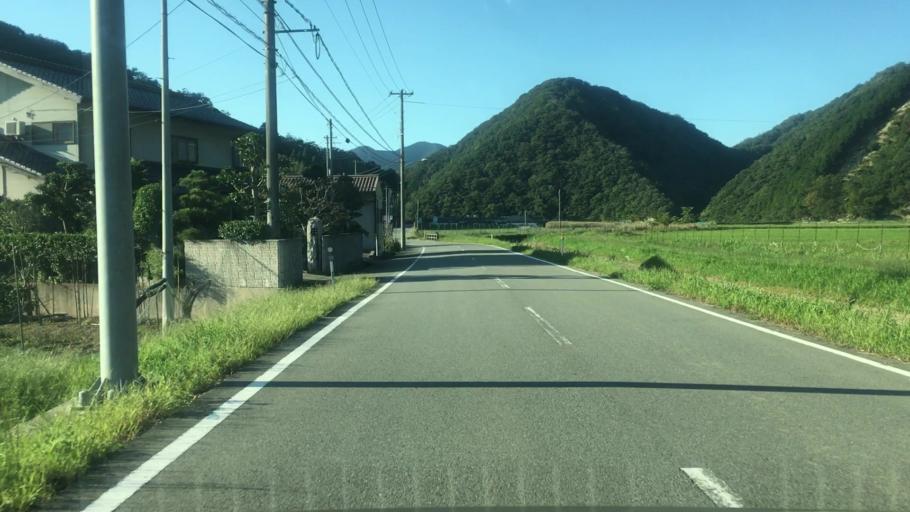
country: JP
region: Hyogo
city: Toyooka
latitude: 35.6115
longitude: 134.8288
